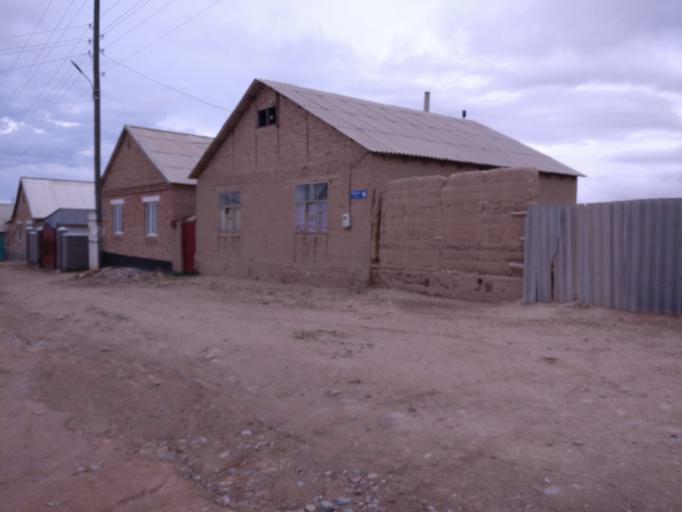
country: KG
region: Ysyk-Koel
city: Bokombayevskoye
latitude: 42.1137
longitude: 76.9818
